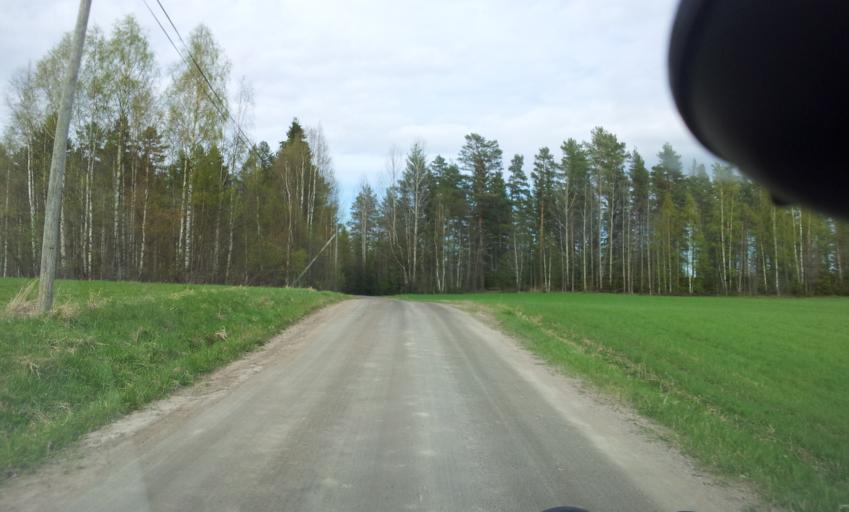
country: SE
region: Gaevleborg
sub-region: Ljusdals Kommun
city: Farila
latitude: 61.7961
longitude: 15.9065
